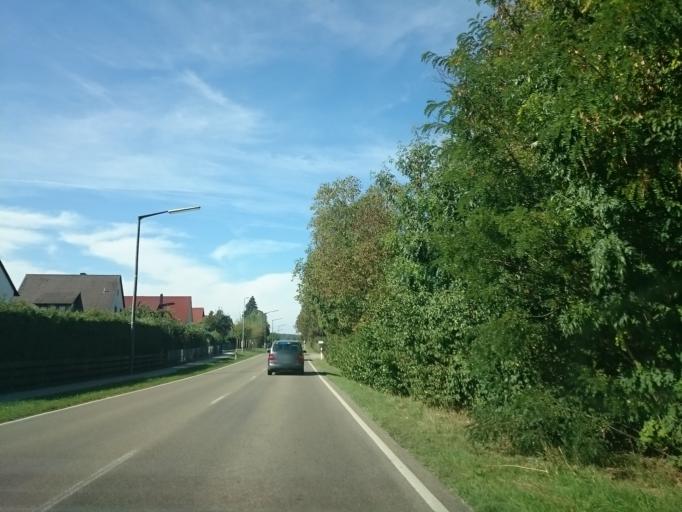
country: DE
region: Bavaria
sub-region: Regierungsbezirk Mittelfranken
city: Heideck
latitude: 49.1360
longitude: 11.1365
